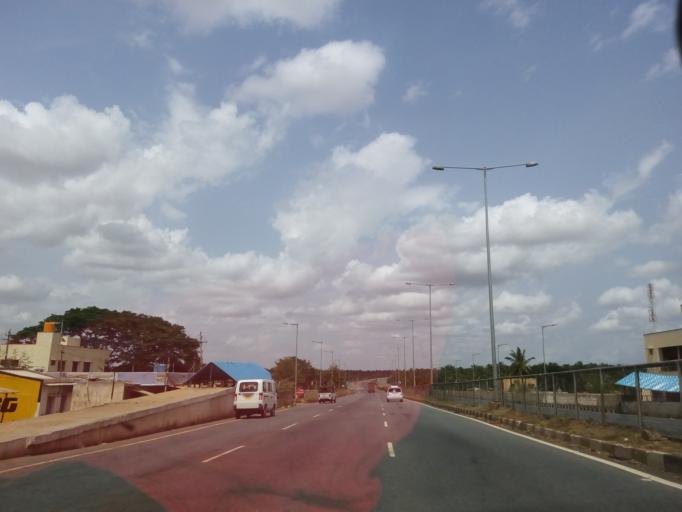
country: IN
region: Karnataka
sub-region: Chitradurga
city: Hiriyur
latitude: 13.8379
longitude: 76.7468
